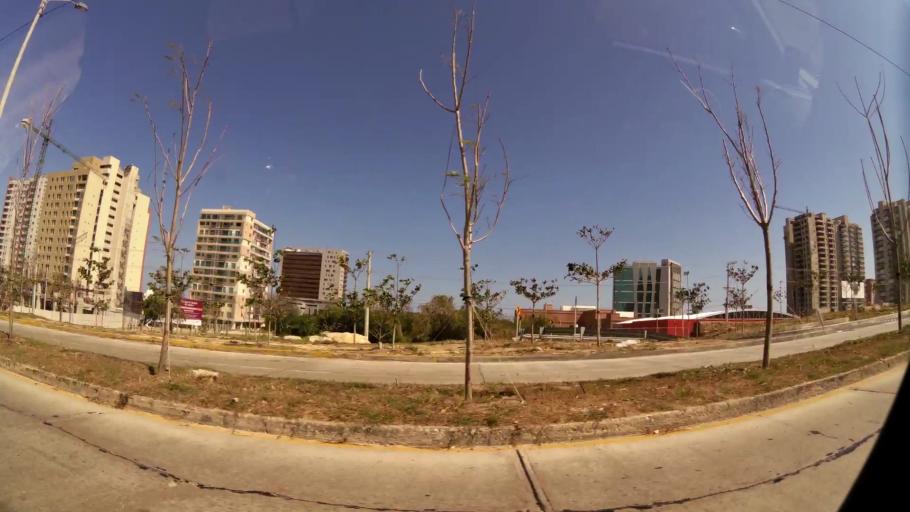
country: CO
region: Atlantico
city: Barranquilla
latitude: 11.0160
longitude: -74.8395
